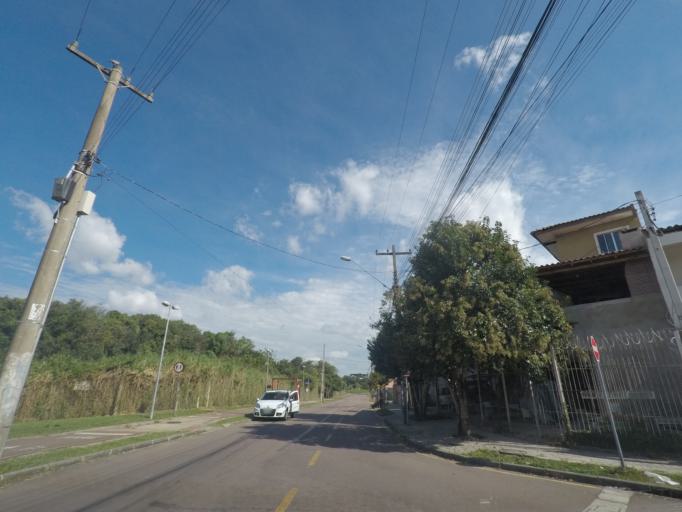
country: BR
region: Parana
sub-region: Curitiba
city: Curitiba
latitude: -25.4801
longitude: -49.3356
